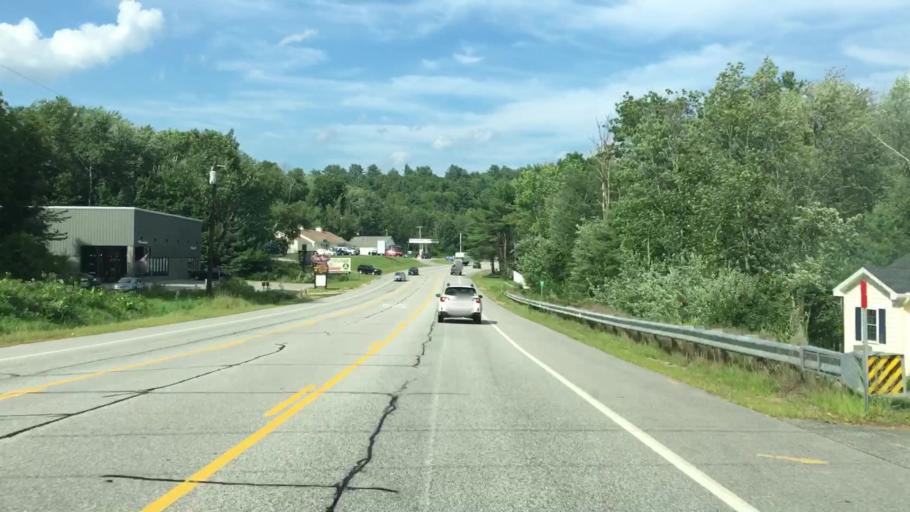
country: US
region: New Hampshire
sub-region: Belknap County
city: Sanbornton
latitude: 43.4819
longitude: -71.5393
